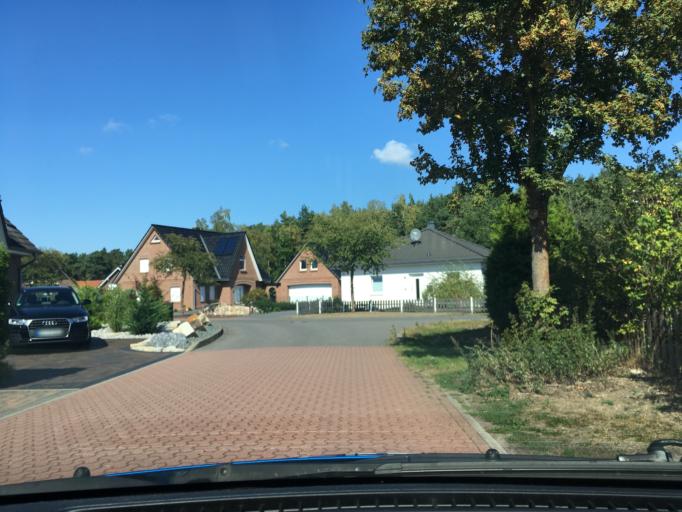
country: DE
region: Lower Saxony
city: Winsen
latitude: 52.6924
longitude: 9.9172
